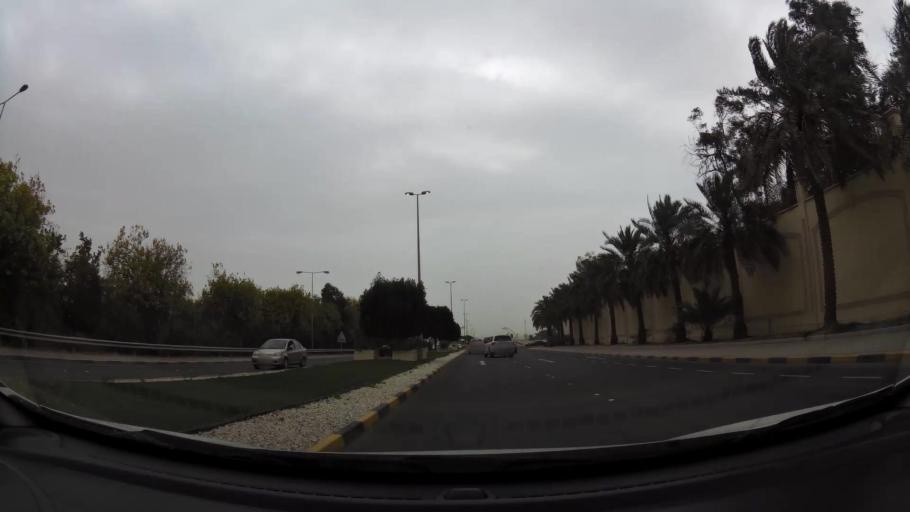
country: BH
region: Northern
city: Ar Rifa'
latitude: 26.1403
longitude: 50.5431
